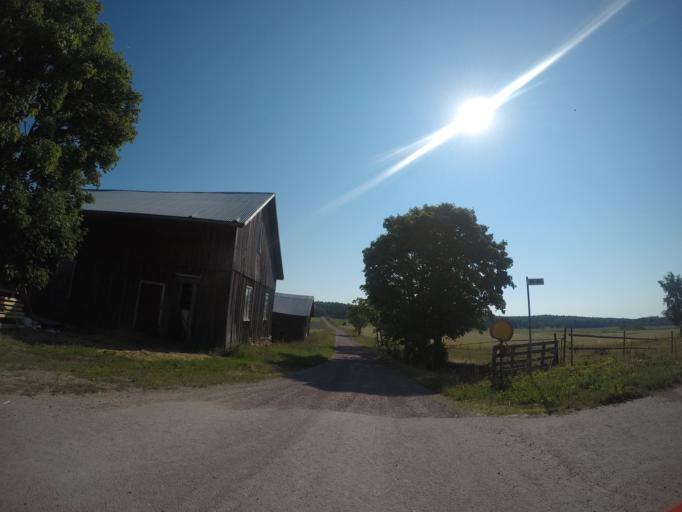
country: AX
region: Alands landsbygd
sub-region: Jomala
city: Jomala
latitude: 60.2042
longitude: 19.9753
